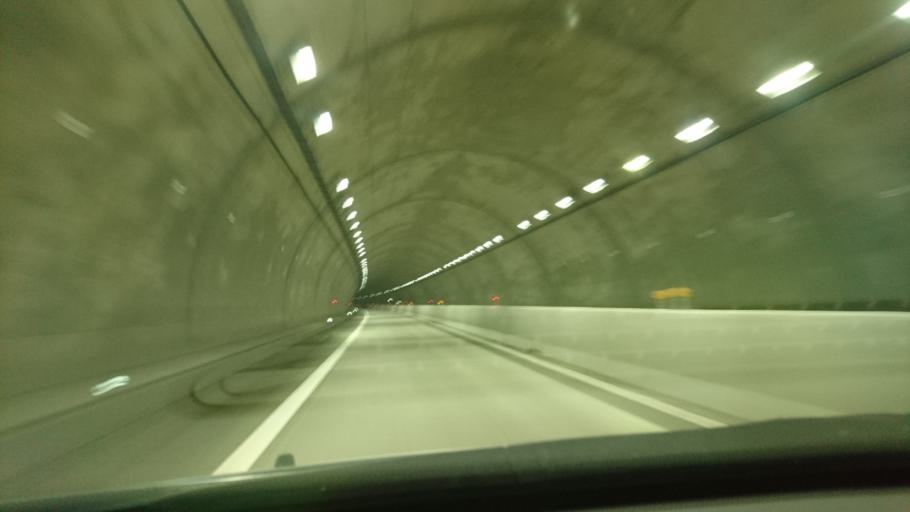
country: JP
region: Iwate
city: Miyako
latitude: 39.8257
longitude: 141.9632
